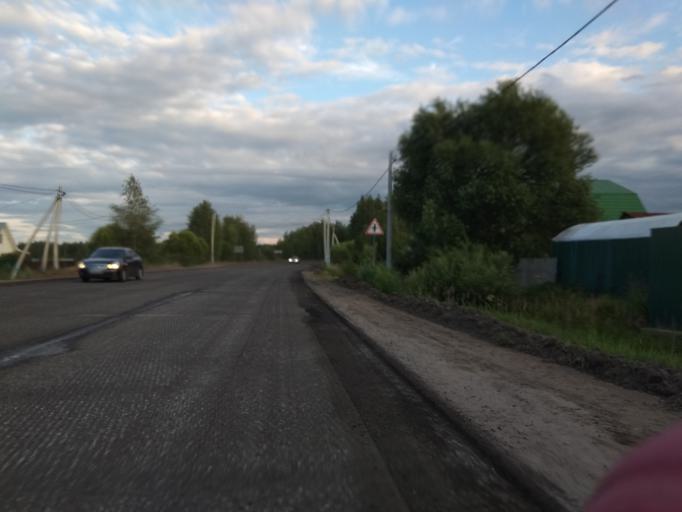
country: RU
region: Moskovskaya
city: Misheronskiy
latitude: 55.6489
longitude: 39.7565
